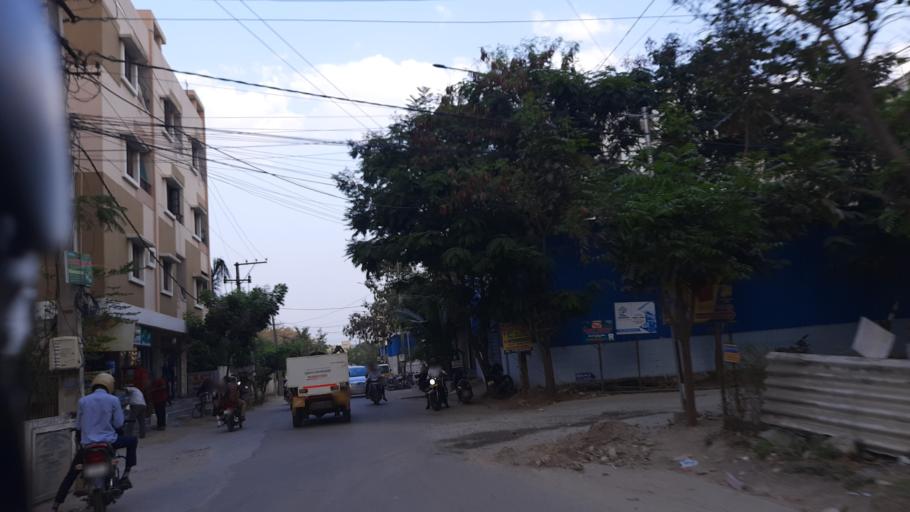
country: IN
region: Telangana
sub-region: Rangareddi
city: Kukatpalli
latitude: 17.4934
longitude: 78.4221
